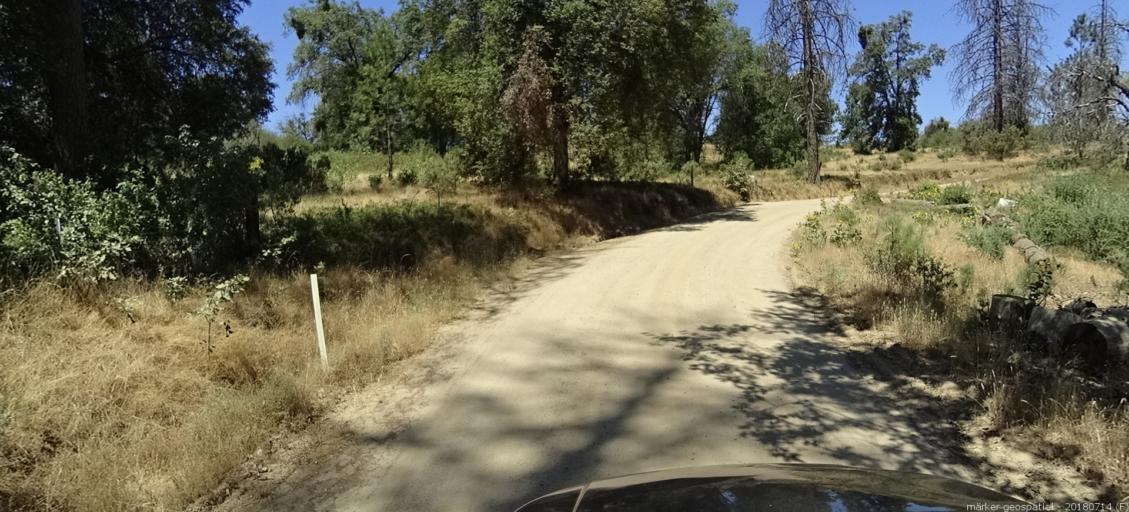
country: US
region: California
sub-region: Madera County
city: Ahwahnee
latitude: 37.3940
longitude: -119.6913
